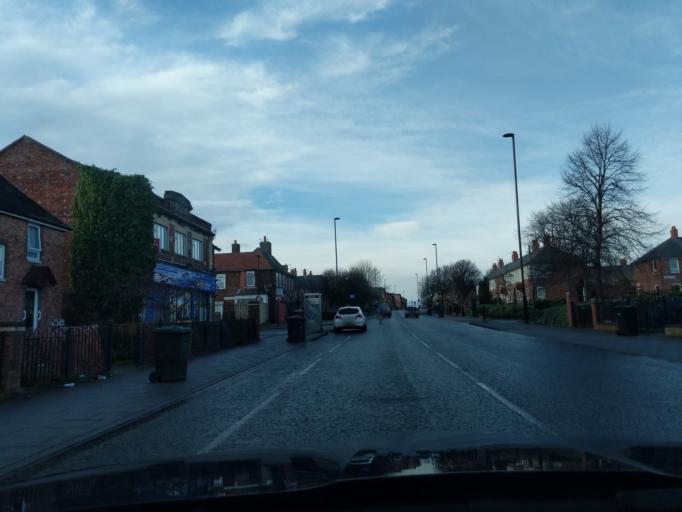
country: GB
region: England
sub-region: Gateshead
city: Felling
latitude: 54.9651
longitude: -1.5584
